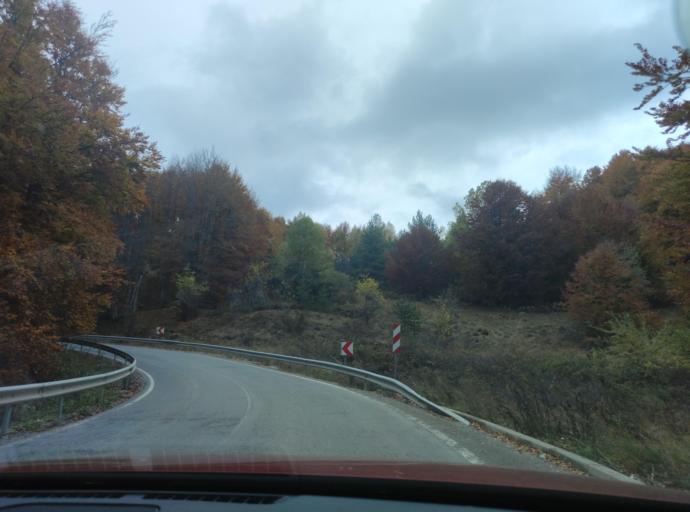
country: BG
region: Sofiya
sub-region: Obshtina Godech
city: Godech
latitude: 43.1067
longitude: 23.1097
